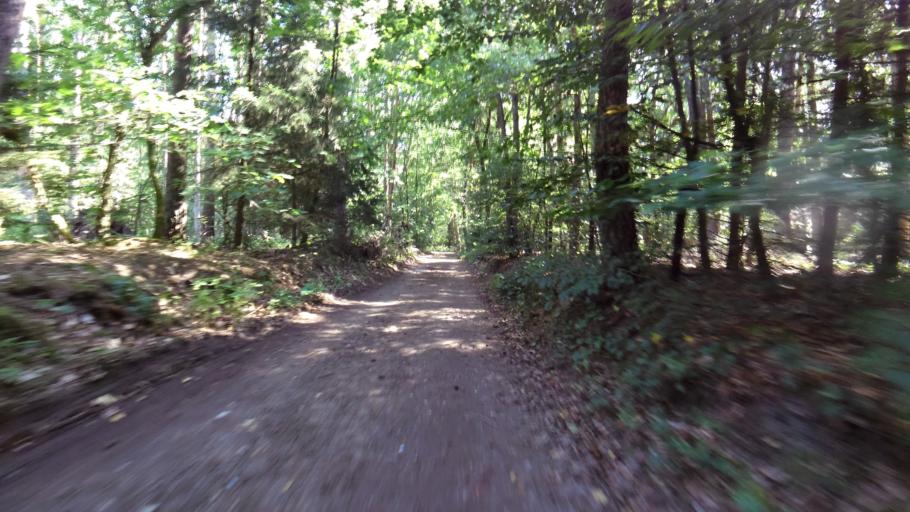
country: NL
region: Gelderland
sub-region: Gemeente Renkum
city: Renkum
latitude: 52.0079
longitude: 5.7316
